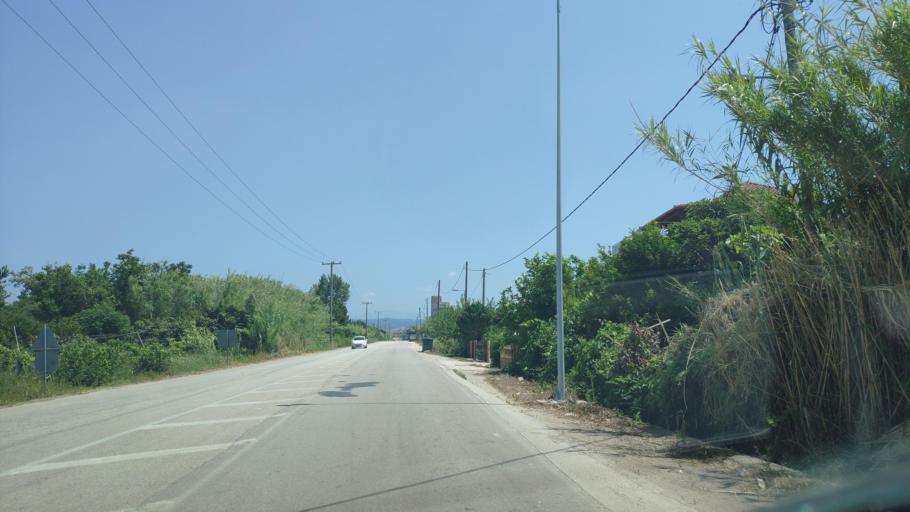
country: GR
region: Epirus
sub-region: Nomos Artas
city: Kostakioi
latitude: 39.1252
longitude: 20.9421
